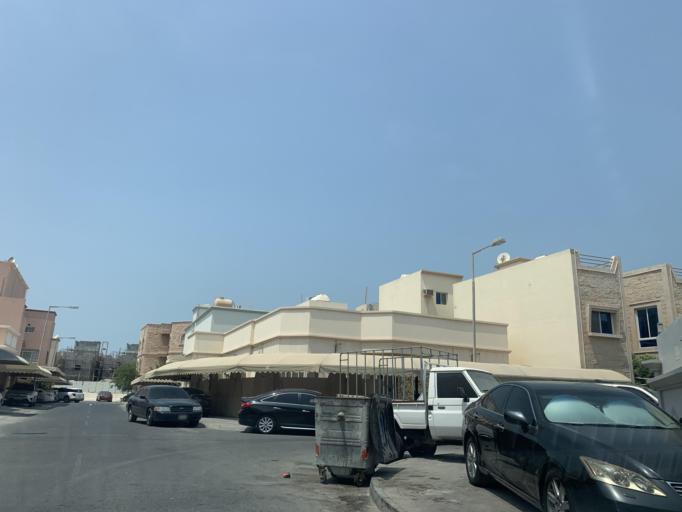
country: BH
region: Muharraq
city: Al Hadd
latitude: 26.2768
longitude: 50.6502
